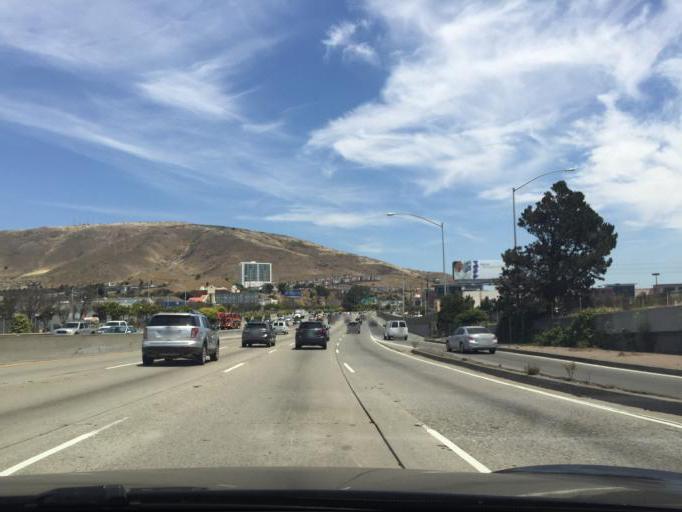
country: US
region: California
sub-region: San Mateo County
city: South San Francisco
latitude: 37.6561
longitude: -122.4065
